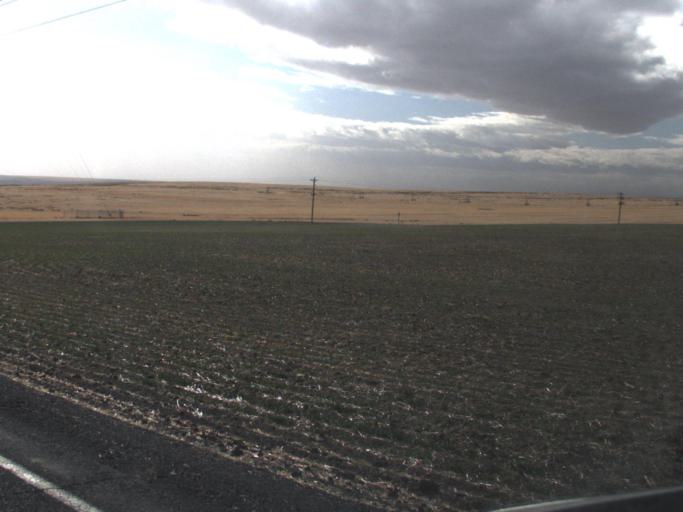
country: US
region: Washington
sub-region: Okanogan County
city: Coulee Dam
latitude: 47.4812
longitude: -118.7848
